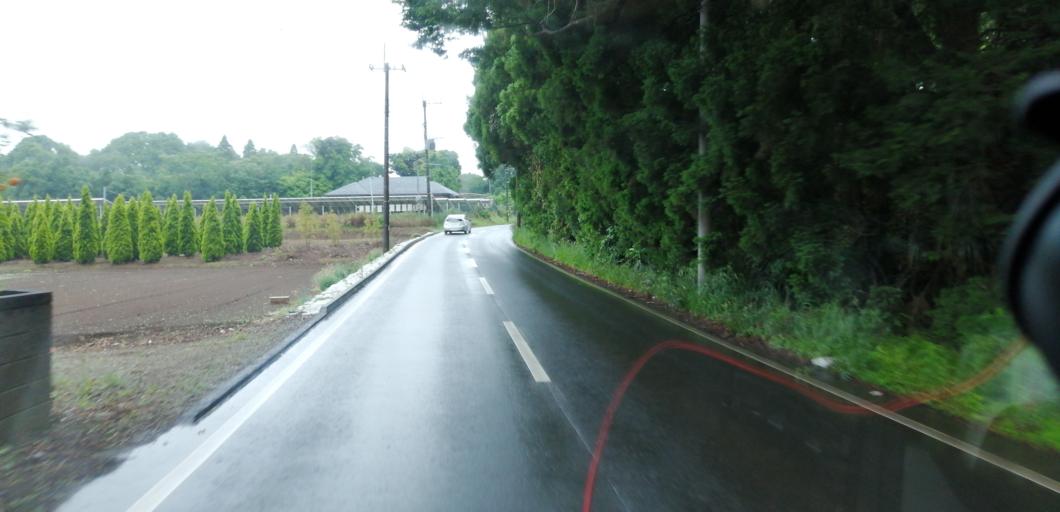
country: JP
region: Chiba
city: Yachimata
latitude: 35.6139
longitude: 140.2877
